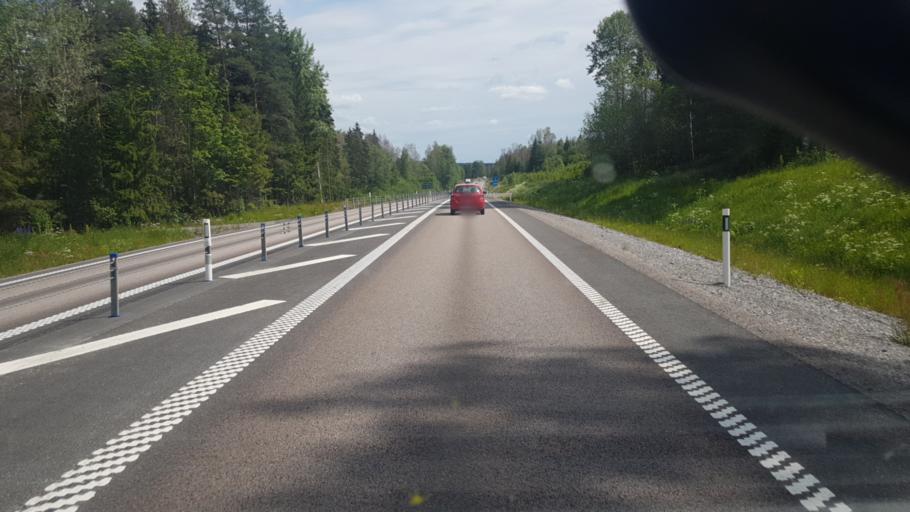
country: SE
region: Vaermland
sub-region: Eda Kommun
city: Amotfors
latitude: 59.7870
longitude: 12.3479
